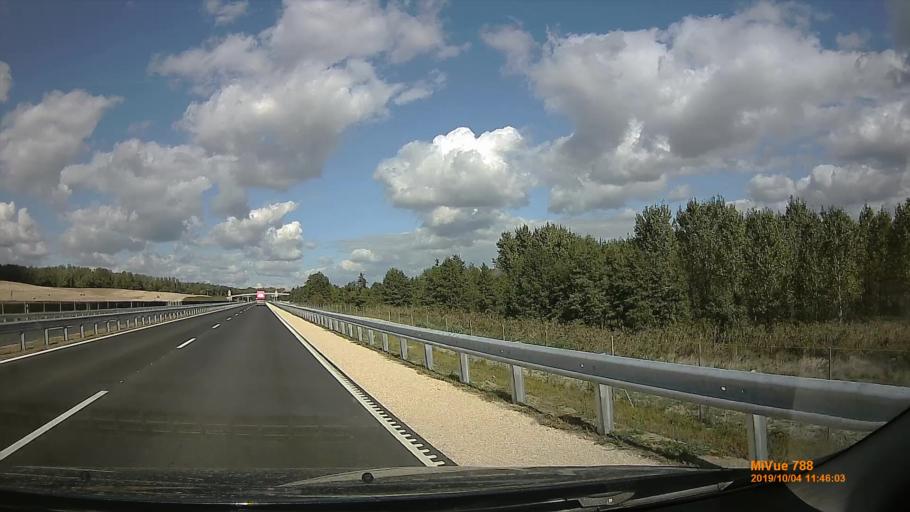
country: HU
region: Somogy
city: Karad
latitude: 46.6326
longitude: 17.7916
